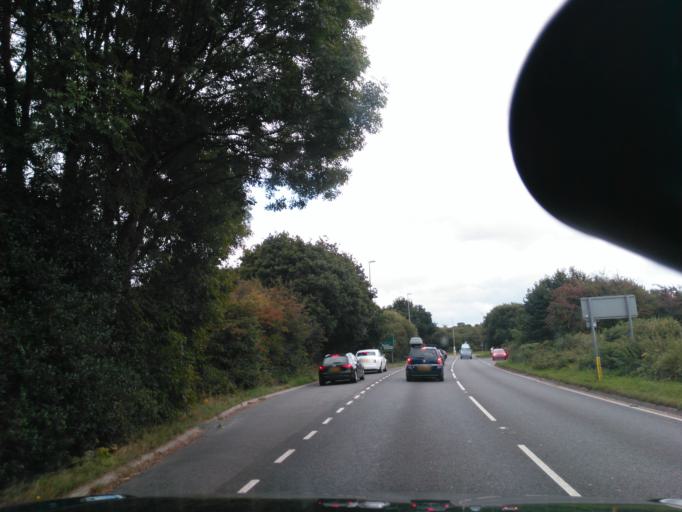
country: GB
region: England
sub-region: Dorset
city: Lytchett Matravers
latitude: 50.7330
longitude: -2.0686
